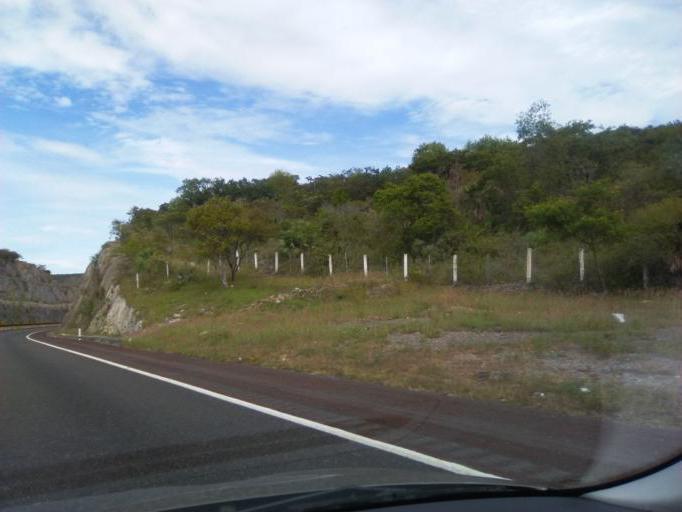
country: MX
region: Guerrero
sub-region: Eduardo Neri
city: Tlanipatla
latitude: 17.8363
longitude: -99.4496
